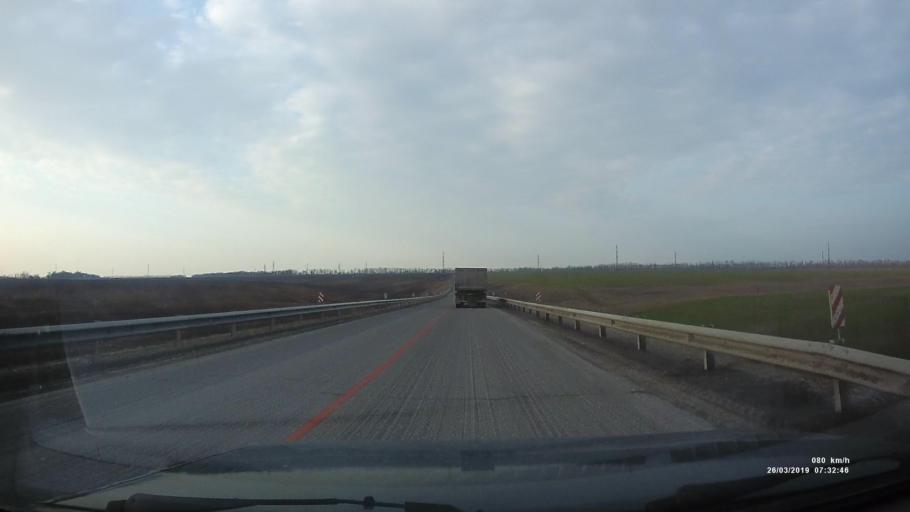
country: RU
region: Rostov
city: Novobessergenovka
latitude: 47.2211
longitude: 38.7746
